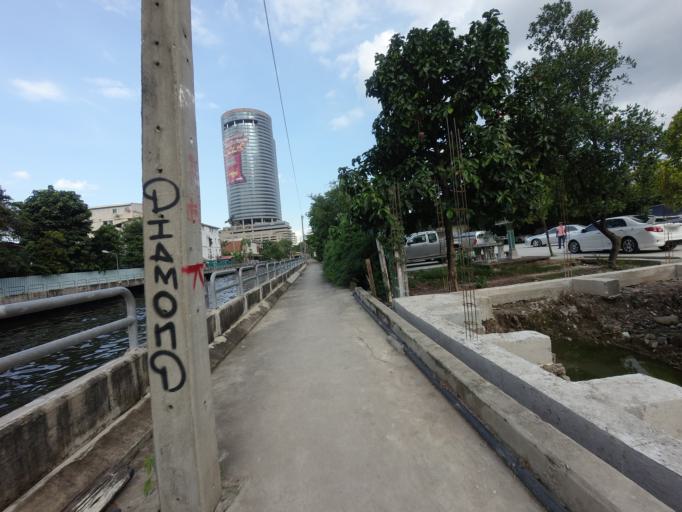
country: TH
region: Bangkok
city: Watthana
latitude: 13.7463
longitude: 100.5706
